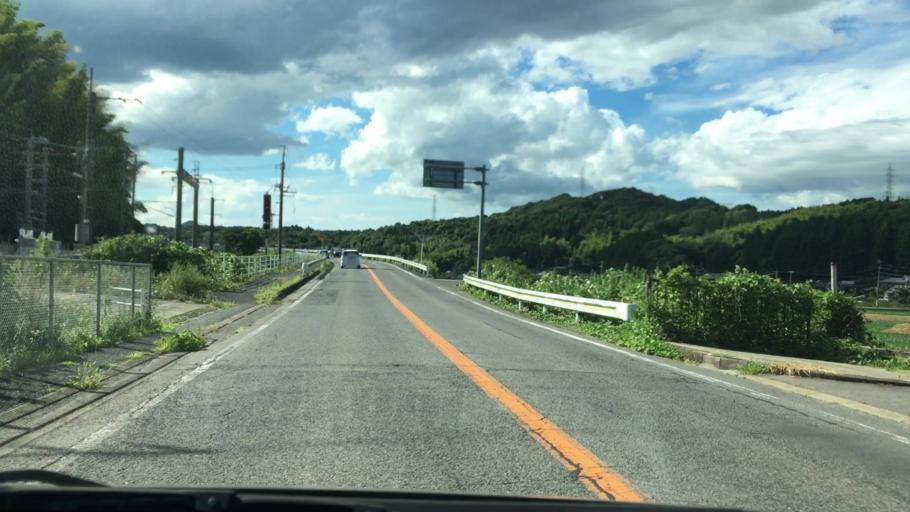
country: JP
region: Saga Prefecture
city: Takeocho-takeo
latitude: 33.1947
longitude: 129.9795
